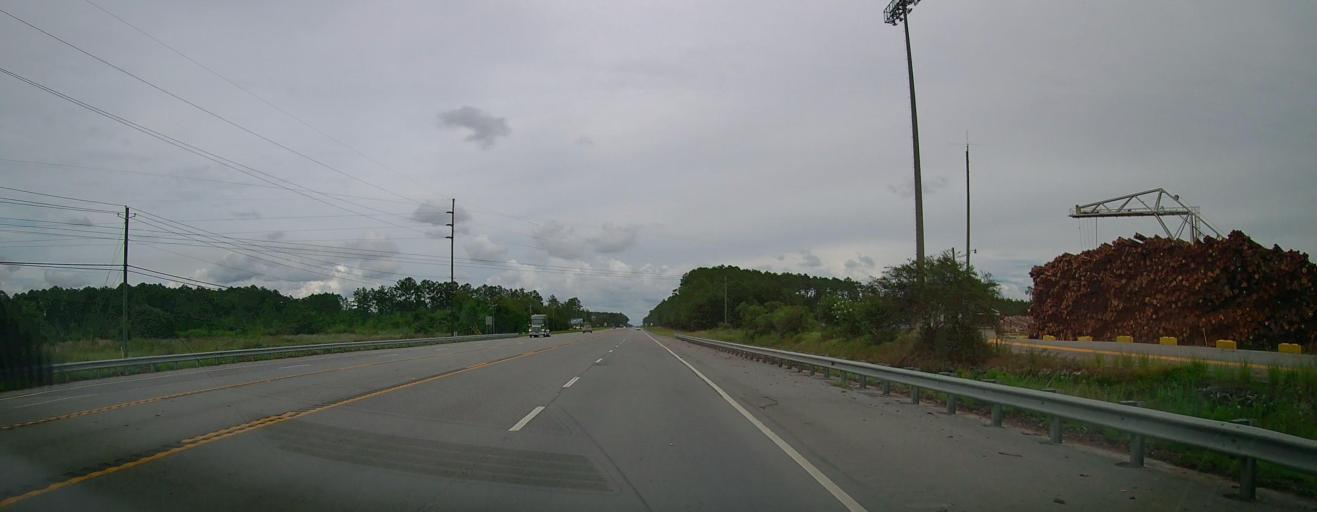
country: US
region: Georgia
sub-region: Appling County
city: Baxley
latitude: 31.7687
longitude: -82.3202
